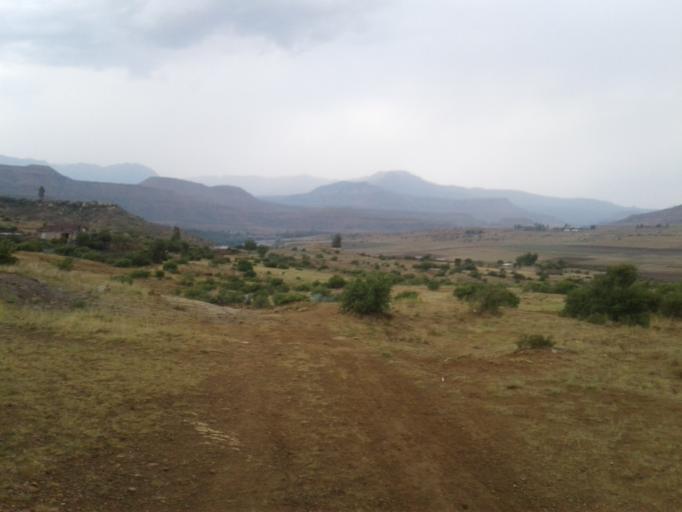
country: LS
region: Quthing
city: Quthing
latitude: -30.3845
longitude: 27.5603
